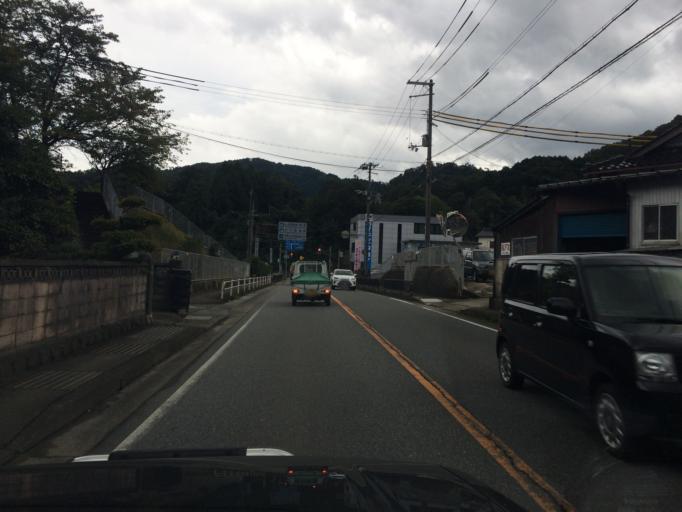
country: JP
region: Hyogo
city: Toyooka
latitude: 35.4049
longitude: 134.7773
